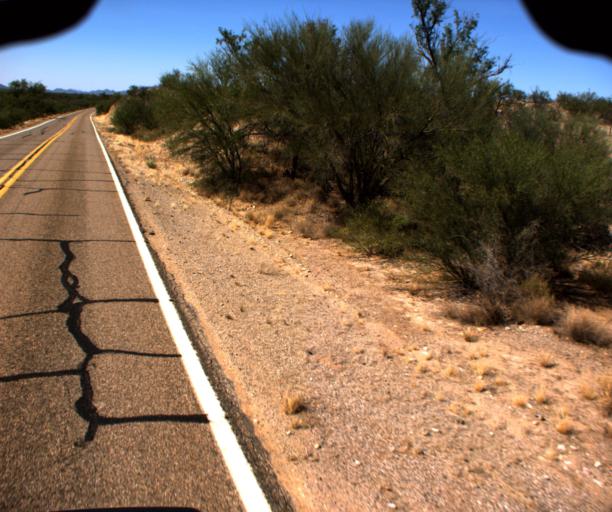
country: US
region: Arizona
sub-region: Pima County
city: Three Points
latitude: 31.9135
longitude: -111.3902
